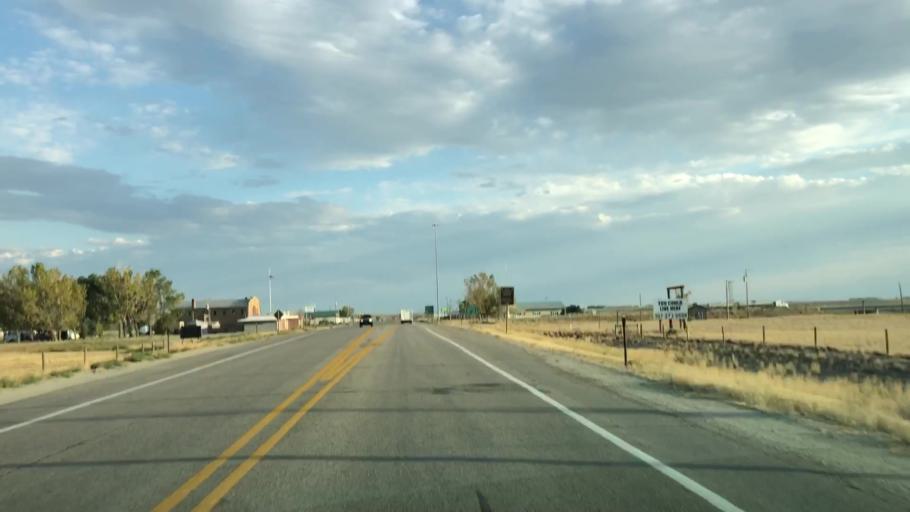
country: US
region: Wyoming
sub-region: Sweetwater County
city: North Rock Springs
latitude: 42.1113
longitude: -109.4499
